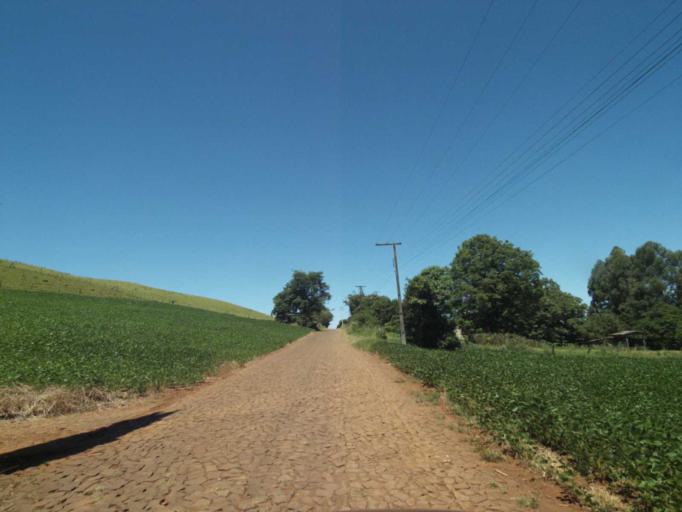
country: BR
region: Parana
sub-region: Coronel Vivida
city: Coronel Vivida
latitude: -25.9658
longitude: -52.8220
